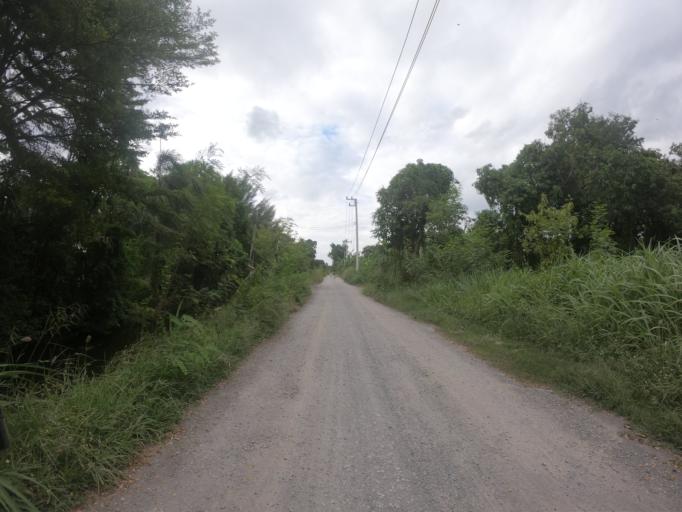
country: TH
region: Pathum Thani
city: Nong Suea
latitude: 14.0751
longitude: 100.8353
